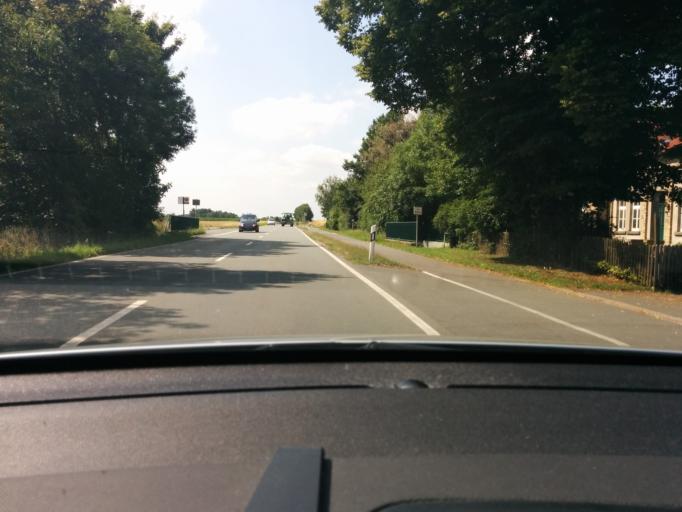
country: DE
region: North Rhine-Westphalia
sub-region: Regierungsbezirk Munster
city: Steinfurt
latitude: 52.1616
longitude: 7.3107
